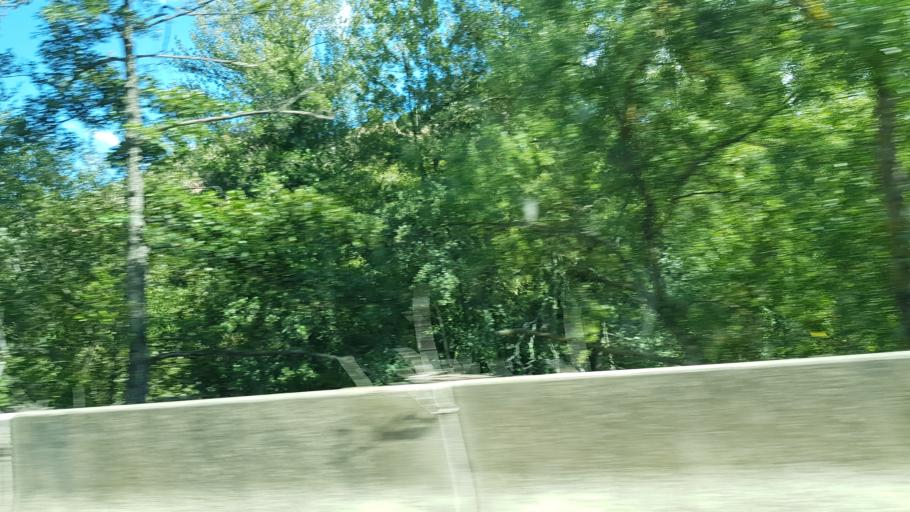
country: ES
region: La Rioja
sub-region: Provincia de La Rioja
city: Viguera
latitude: 42.3134
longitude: -2.5374
